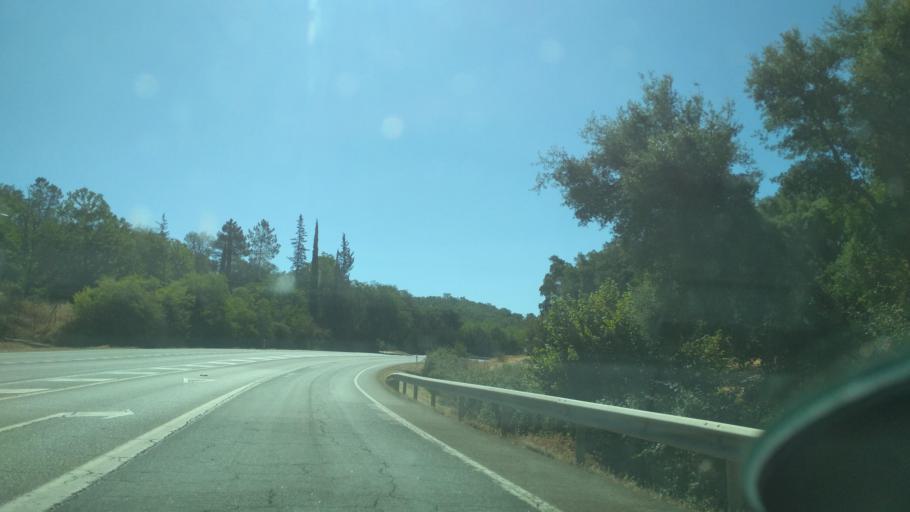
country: ES
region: Andalusia
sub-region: Provincia de Huelva
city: Galaroza
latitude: 37.9211
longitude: -6.6897
